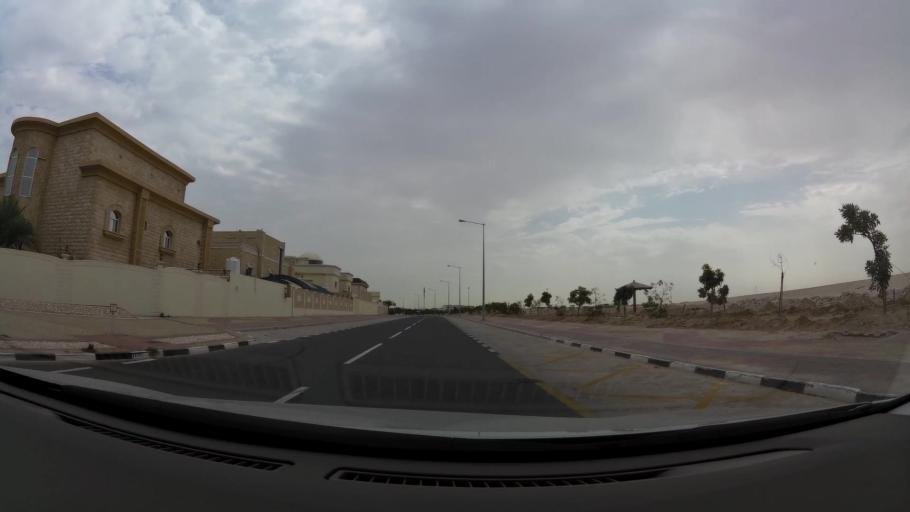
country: QA
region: Baladiyat ad Dawhah
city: Doha
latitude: 25.3519
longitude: 51.4924
